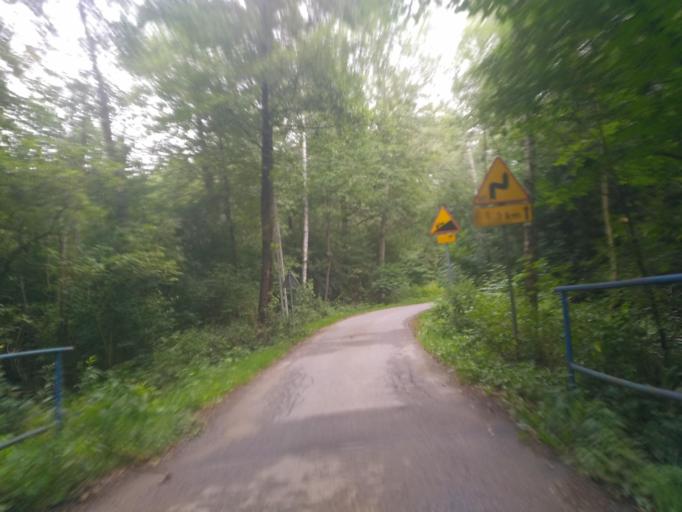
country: PL
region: Subcarpathian Voivodeship
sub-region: Powiat rzeszowski
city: Chmielnik
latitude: 49.9981
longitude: 22.1025
